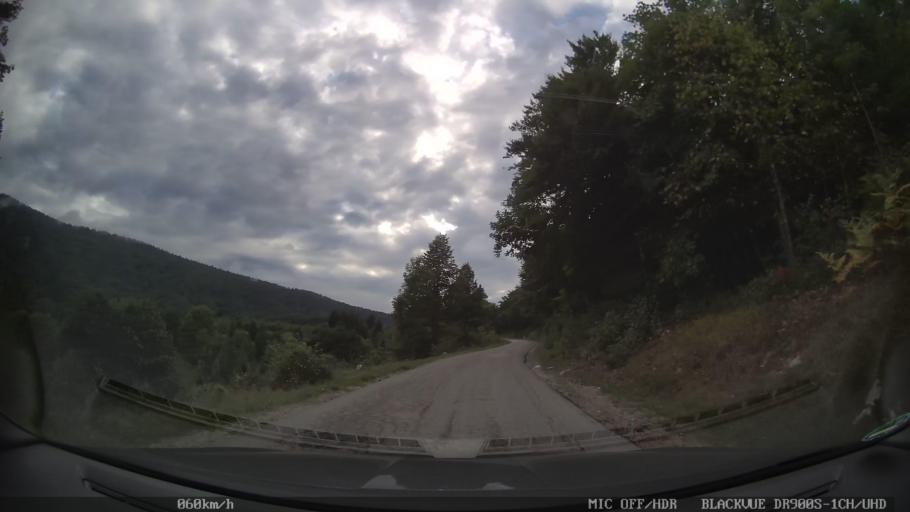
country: HR
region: Licko-Senjska
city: Jezerce
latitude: 44.9280
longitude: 15.5601
